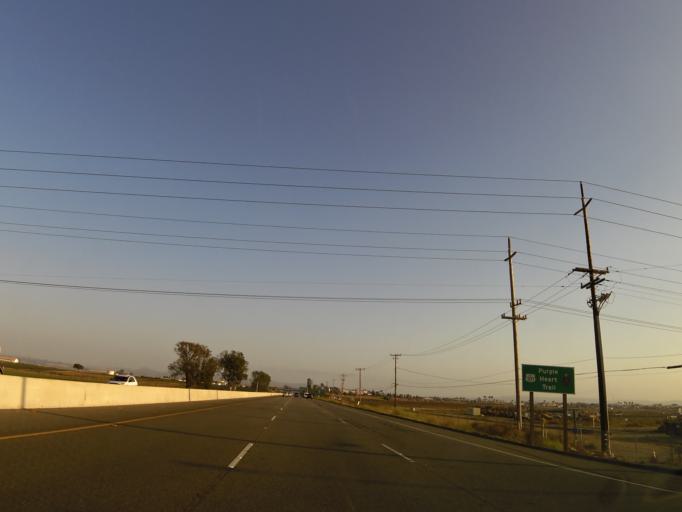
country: US
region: California
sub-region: Santa Barbara County
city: Santa Maria
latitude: 34.9316
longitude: -120.4180
